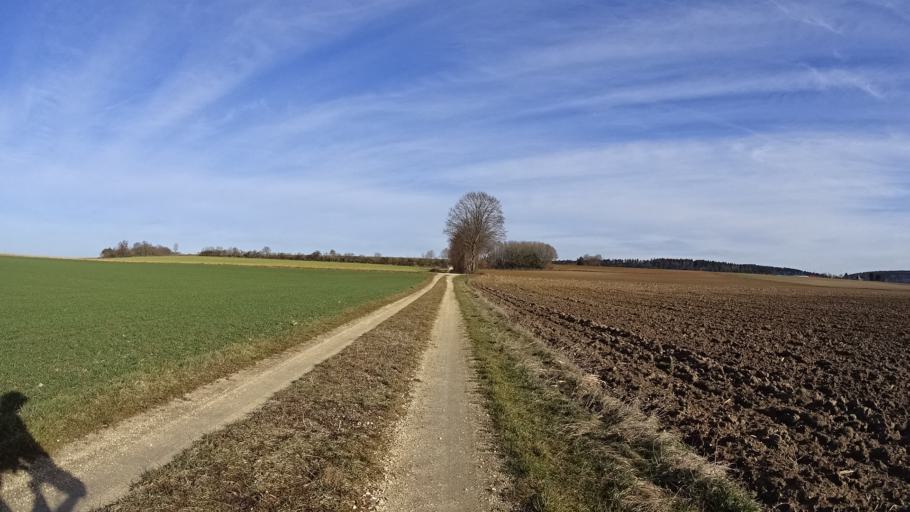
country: DE
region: Bavaria
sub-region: Upper Bavaria
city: Eitensheim
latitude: 48.8328
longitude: 11.3415
